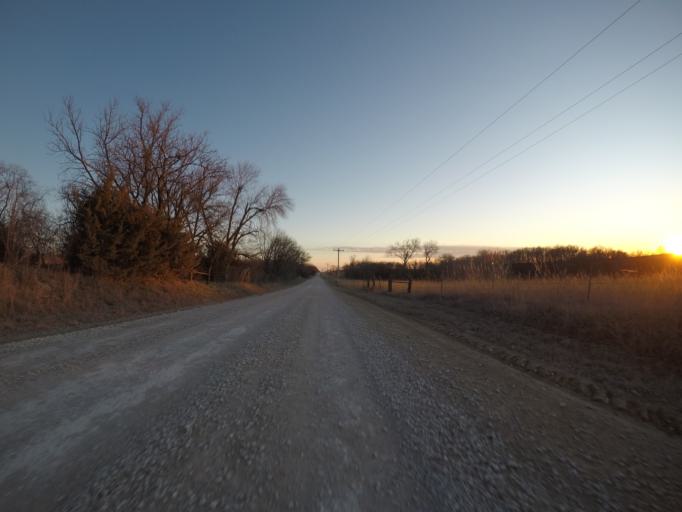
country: US
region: Kansas
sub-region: Riley County
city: Manhattan
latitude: 39.2496
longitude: -96.4827
